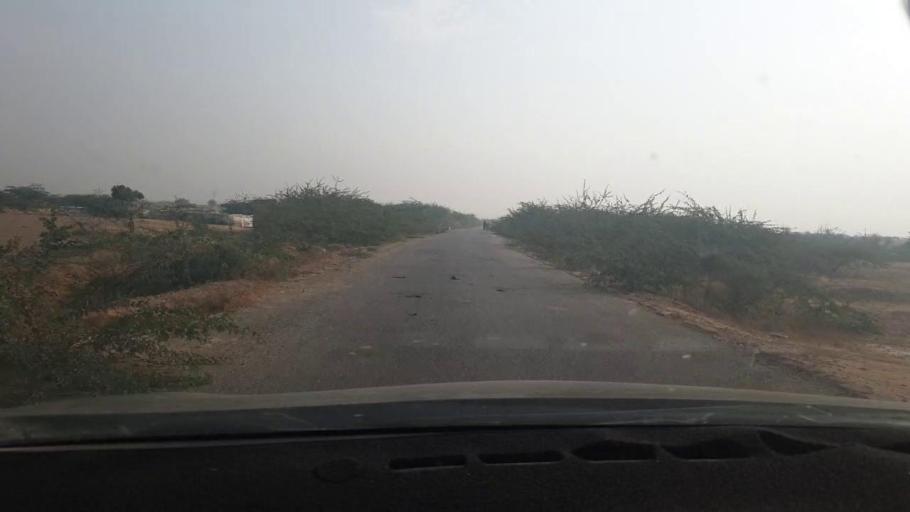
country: PK
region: Sindh
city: Malir Cantonment
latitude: 24.9558
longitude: 67.4495
